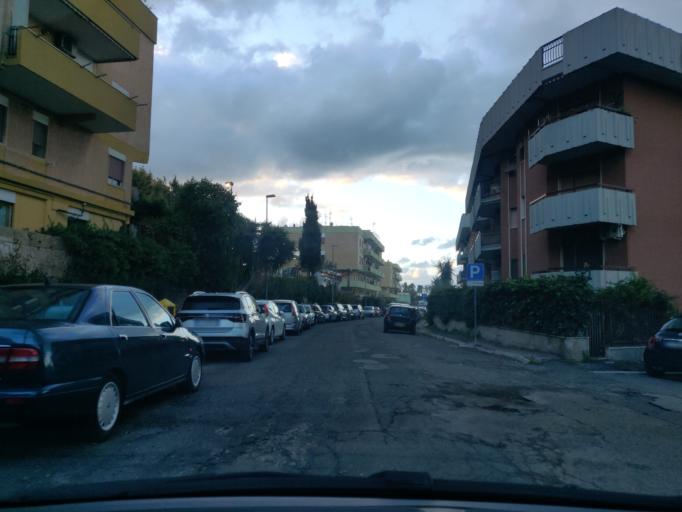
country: IT
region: Latium
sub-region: Citta metropolitana di Roma Capitale
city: Civitavecchia
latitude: 42.0876
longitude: 11.8041
